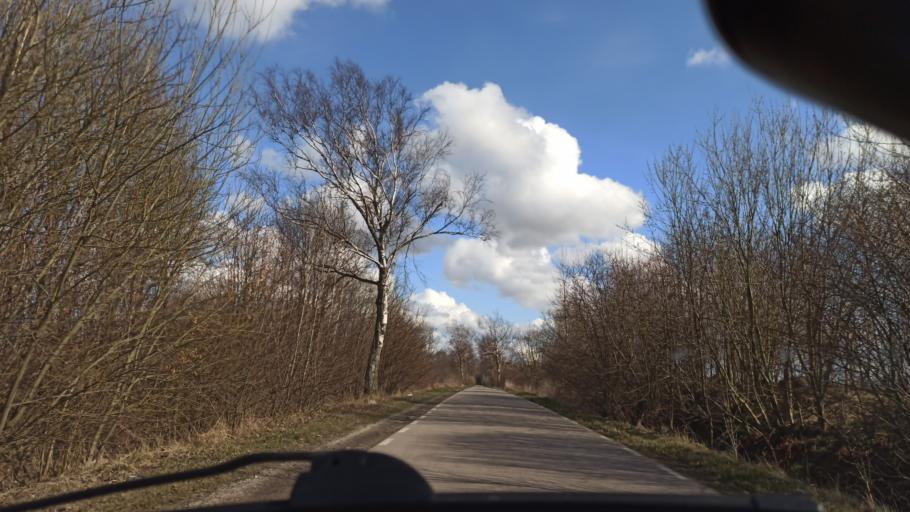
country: PL
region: Warmian-Masurian Voivodeship
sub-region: Powiat elblaski
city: Tolkmicko
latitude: 54.2648
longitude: 19.4841
